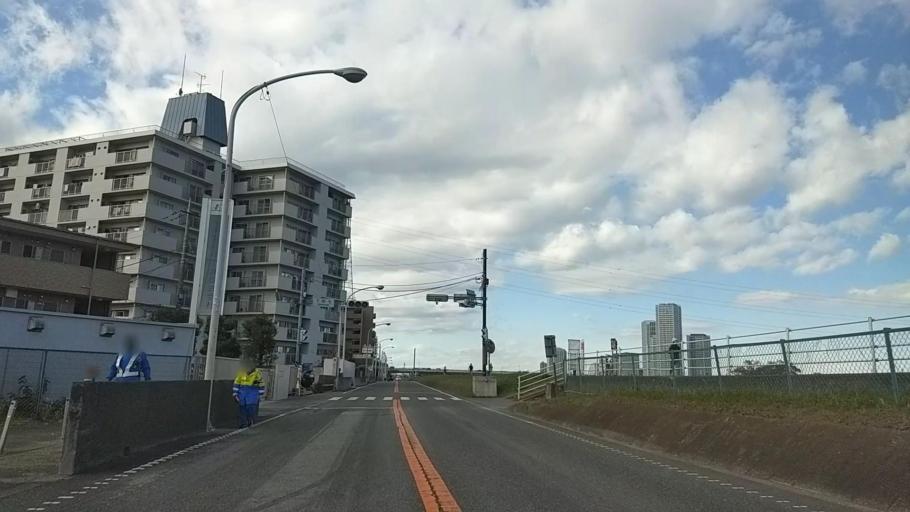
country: JP
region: Tokyo
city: Tokyo
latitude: 35.5984
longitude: 139.6384
